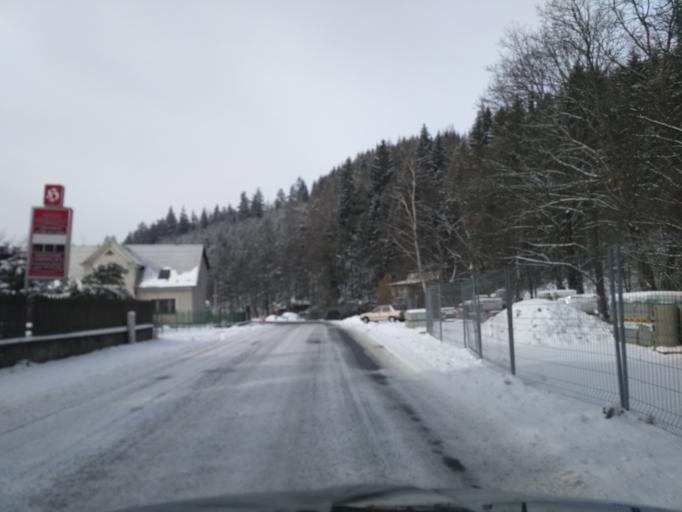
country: CZ
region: Zlin
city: Valasska Bystrice
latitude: 49.4197
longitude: 18.0965
